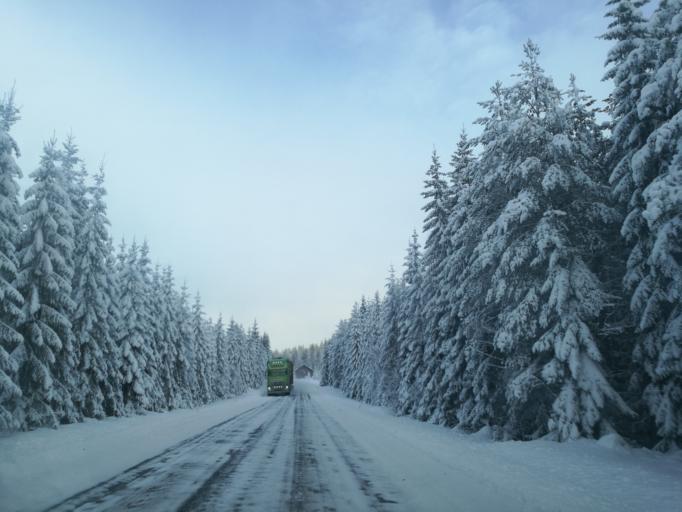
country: SE
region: Vaermland
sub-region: Torsby Kommun
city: Torsby
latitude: 60.6061
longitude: 12.7265
